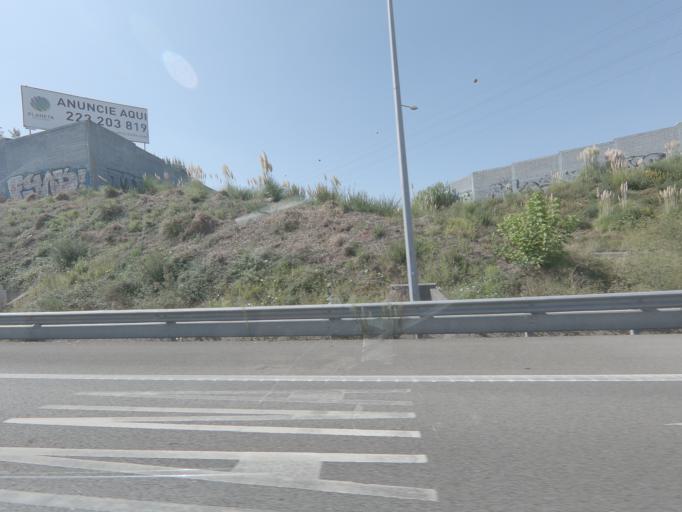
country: PT
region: Porto
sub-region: Matosinhos
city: Guifoes
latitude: 41.1922
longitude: -8.6664
